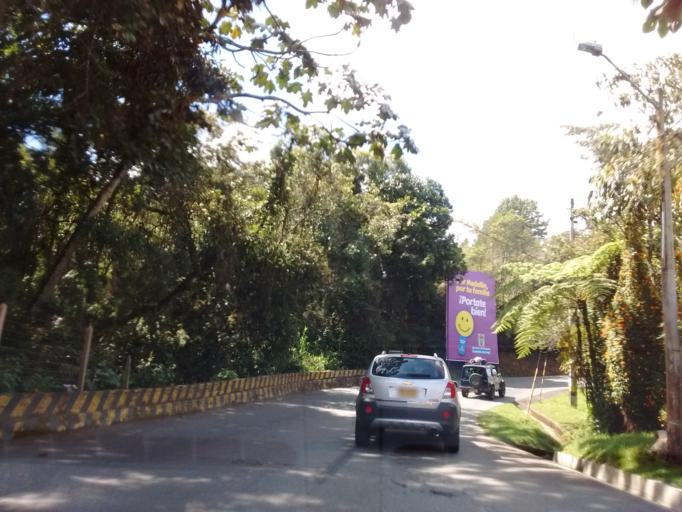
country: CO
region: Antioquia
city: Medellin
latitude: 6.2218
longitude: -75.5019
